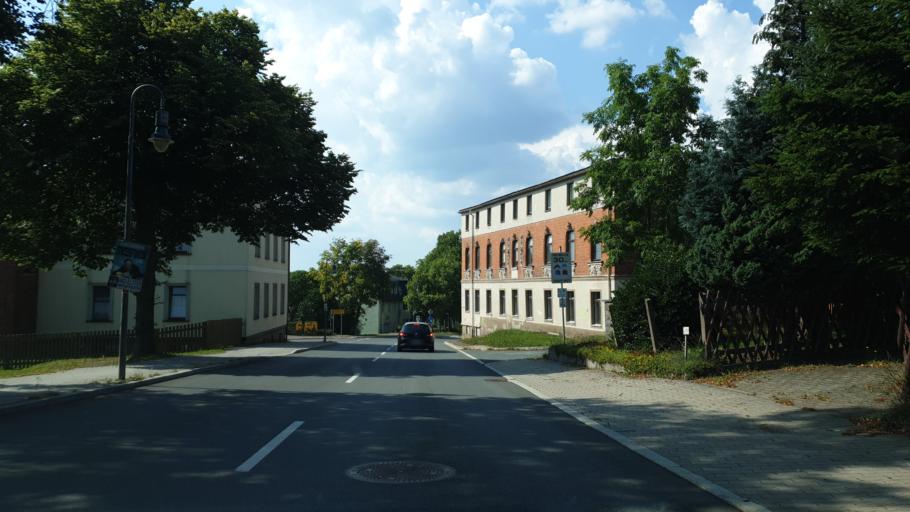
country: DE
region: Saxony
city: Pohl
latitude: 50.3953
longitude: 12.3392
